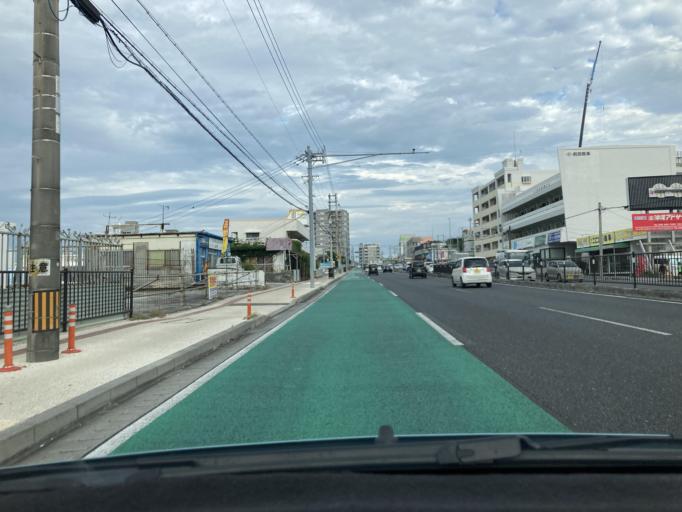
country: JP
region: Okinawa
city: Ginowan
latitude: 26.2773
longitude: 127.7444
